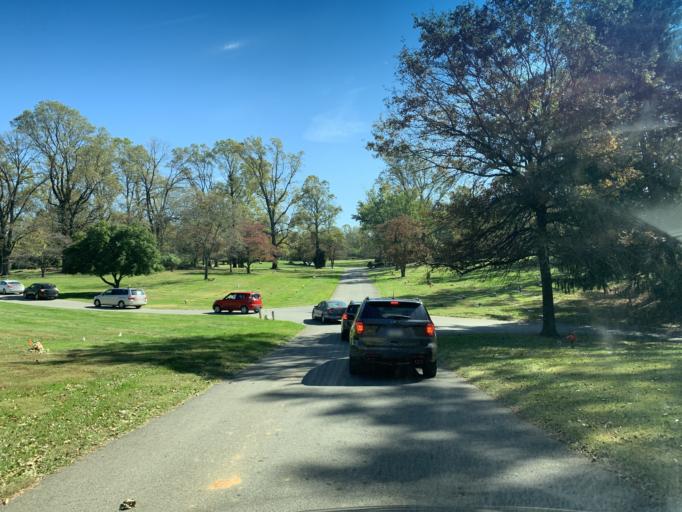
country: US
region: Pennsylvania
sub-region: Berks County
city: Mount Penn
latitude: 40.3110
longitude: -75.8914
